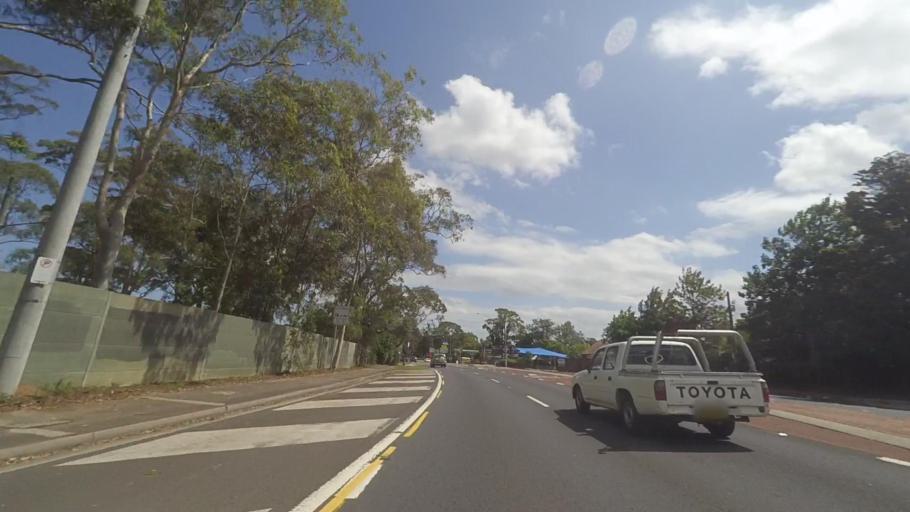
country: AU
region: New South Wales
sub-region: The Hills Shire
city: West Pennant
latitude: -33.7621
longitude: 151.0481
